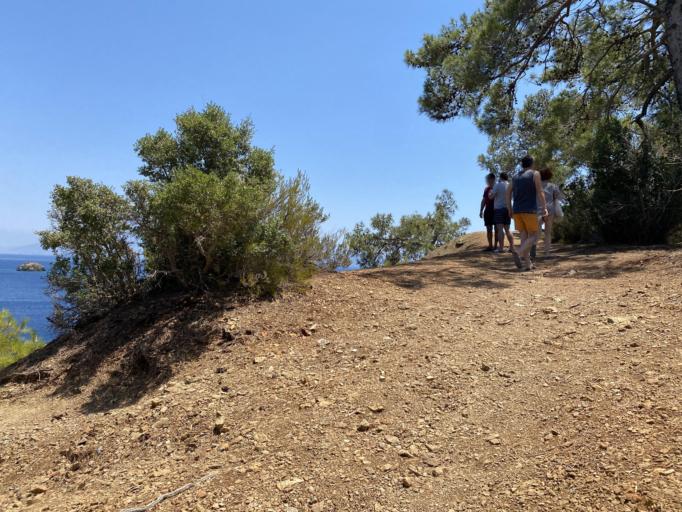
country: TR
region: Mugla
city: Goecek
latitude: 36.7072
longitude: 28.9347
